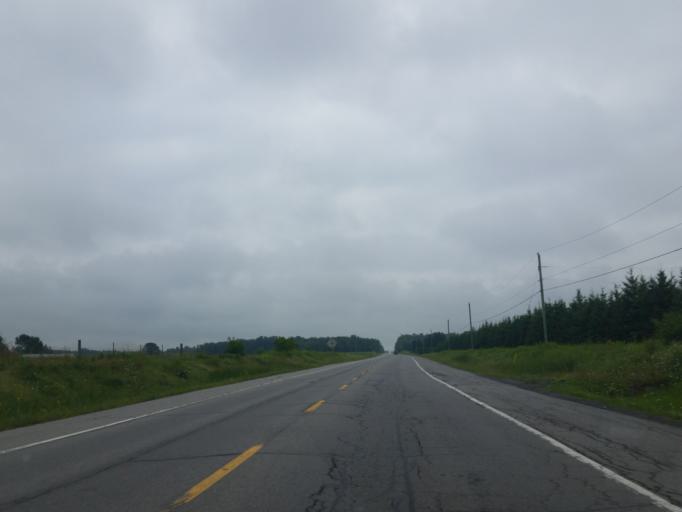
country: CA
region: Ontario
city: Clarence-Rockland
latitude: 45.3698
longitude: -75.3785
